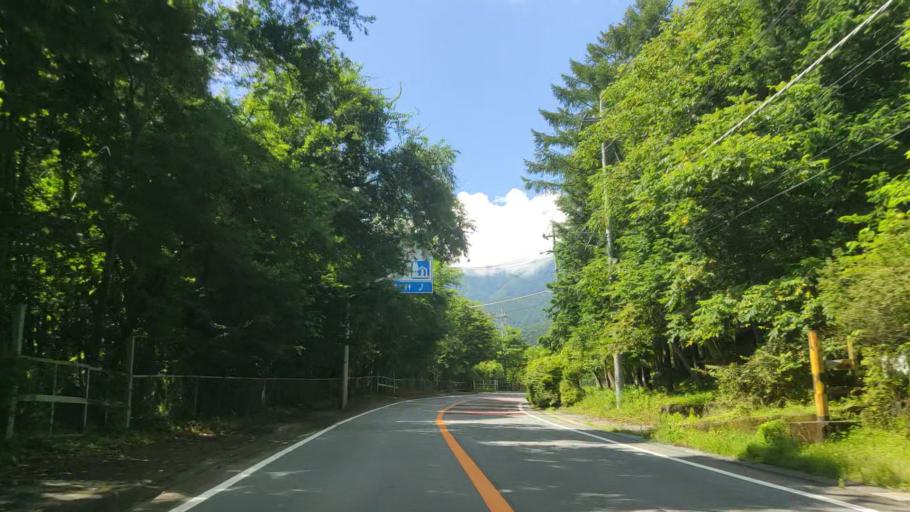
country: JP
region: Yamanashi
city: Enzan
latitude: 35.8566
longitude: 138.7571
